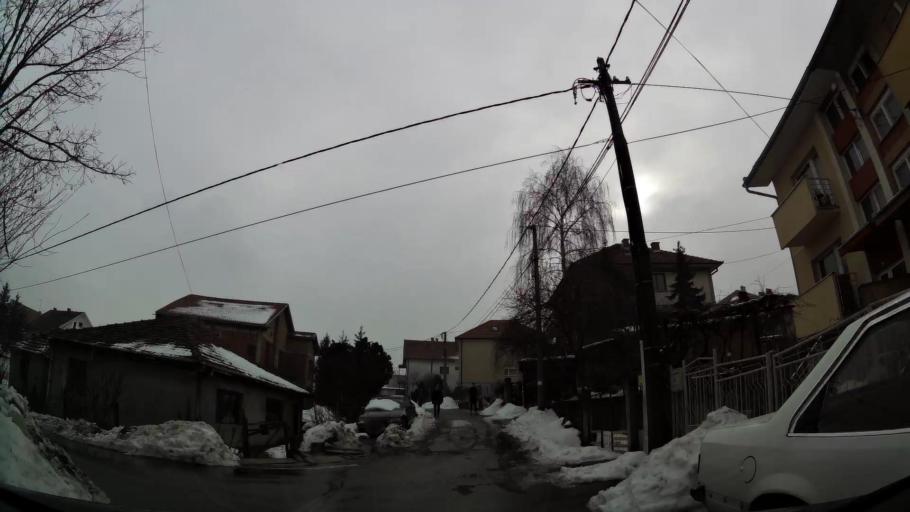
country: RS
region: Central Serbia
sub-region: Belgrade
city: Zvezdara
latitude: 44.7582
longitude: 20.5305
